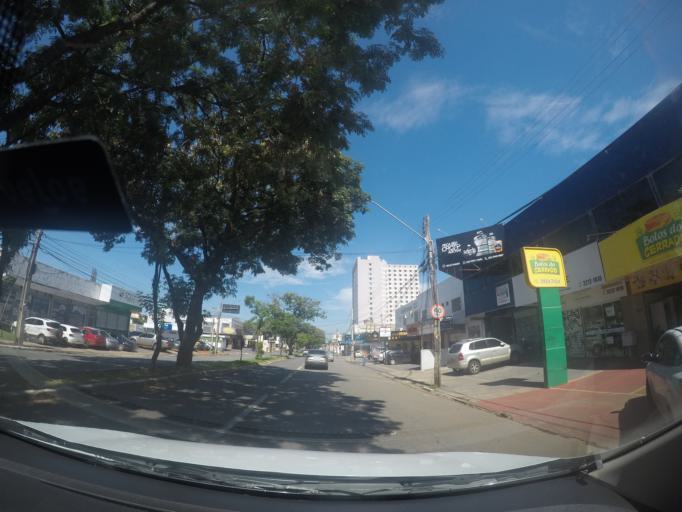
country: BR
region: Goias
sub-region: Goiania
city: Goiania
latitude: -16.7075
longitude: -49.2805
